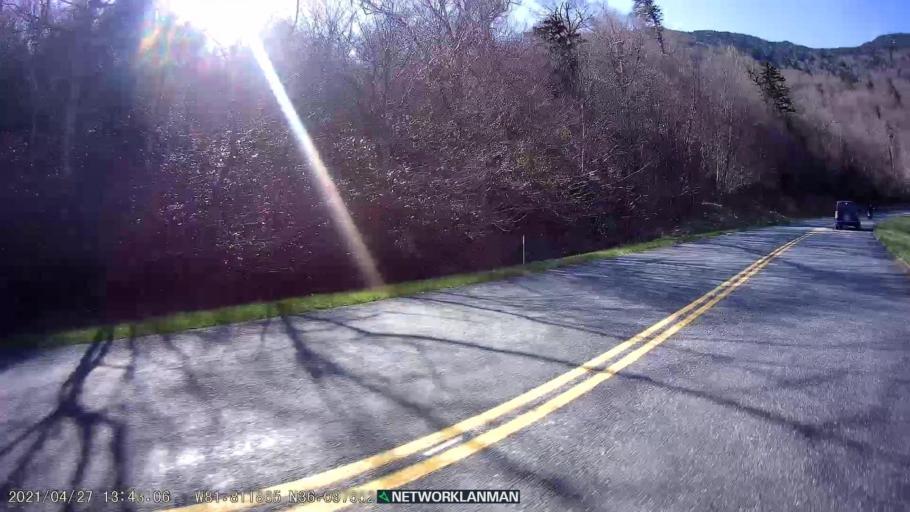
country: US
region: North Carolina
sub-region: Watauga County
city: Foscoe
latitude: 36.0982
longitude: -81.8121
